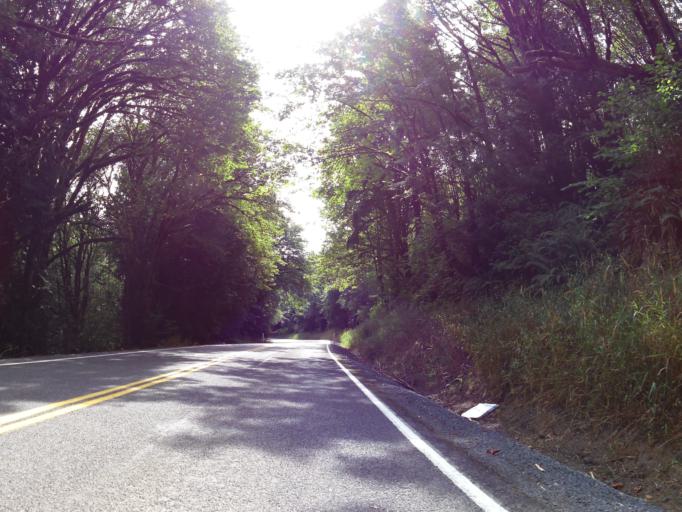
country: US
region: Washington
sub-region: Lewis County
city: Napavine
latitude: 46.5539
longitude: -122.9579
